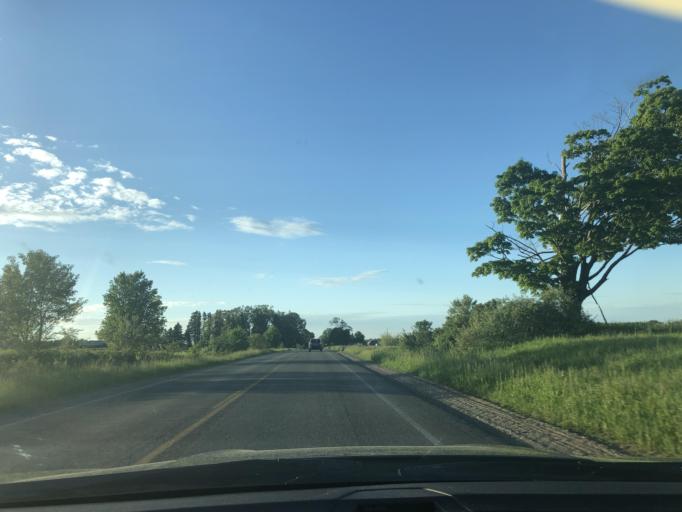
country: US
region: Michigan
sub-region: Missaukee County
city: Lake City
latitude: 44.4175
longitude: -85.0754
